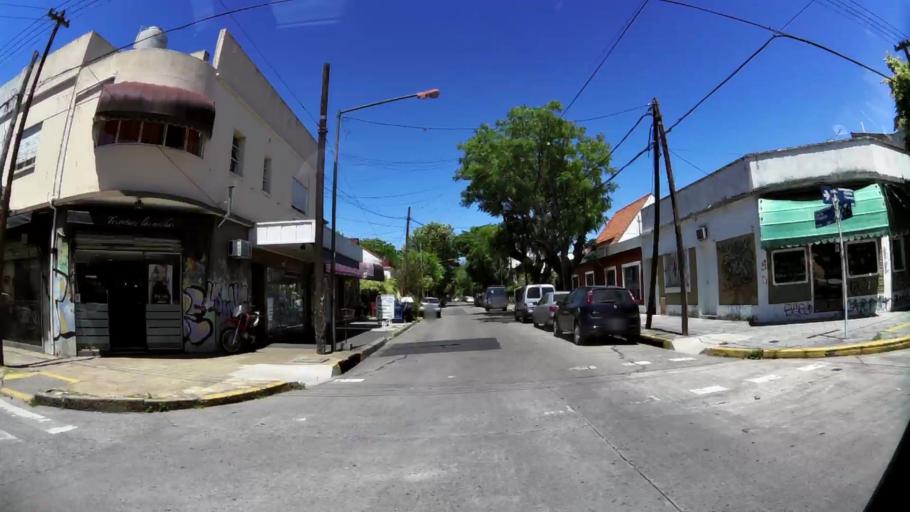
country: AR
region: Buenos Aires
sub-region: Partido de San Isidro
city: San Isidro
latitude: -34.4913
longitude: -58.5043
